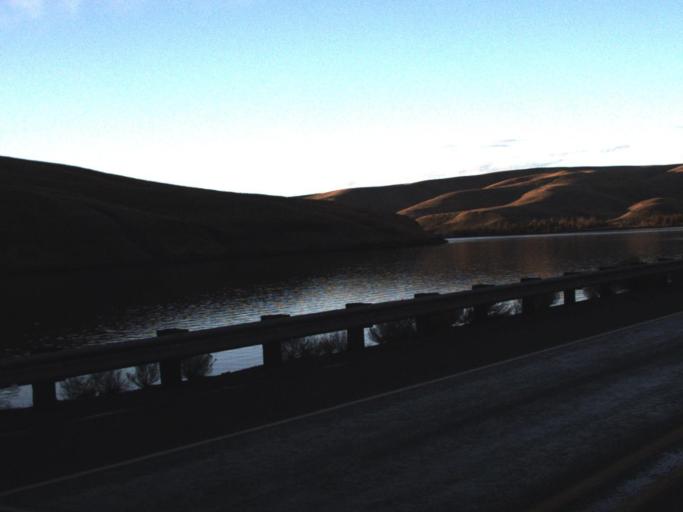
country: US
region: Washington
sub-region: Garfield County
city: Pomeroy
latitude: 46.6158
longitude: -117.7920
